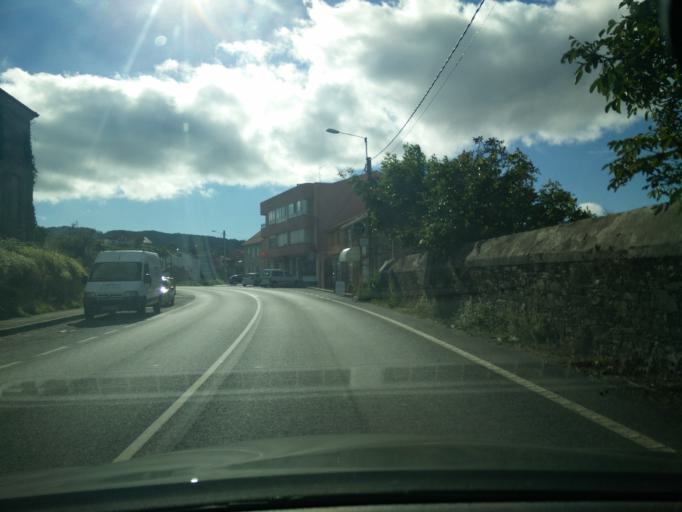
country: ES
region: Galicia
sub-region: Provincia da Coruna
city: Laxe
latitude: 43.2183
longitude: -8.9340
